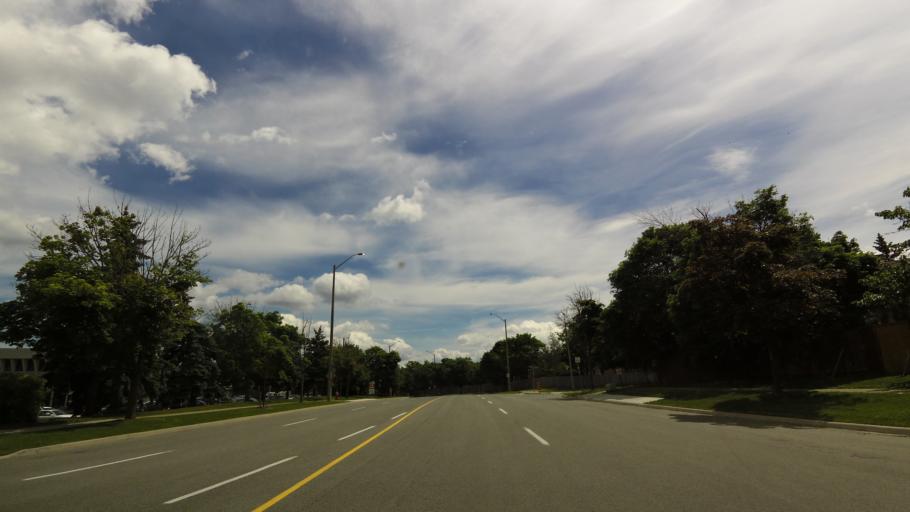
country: CA
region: Ontario
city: Mississauga
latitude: 43.5266
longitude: -79.6533
